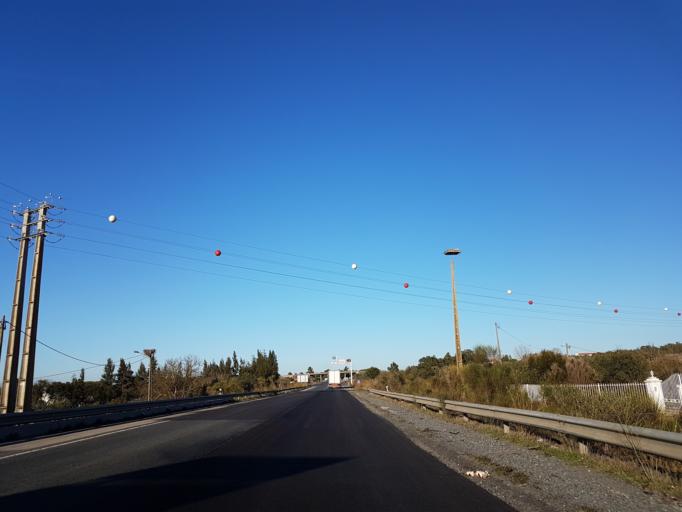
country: PT
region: Setubal
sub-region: Alcacer do Sal
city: Alcacer do Sal
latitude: 38.3770
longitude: -8.5266
